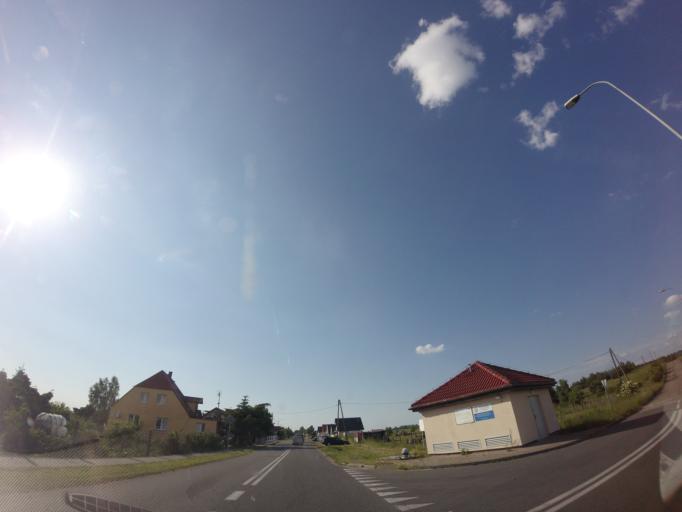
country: PL
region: West Pomeranian Voivodeship
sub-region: Powiat mysliborski
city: Barlinek
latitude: 53.0064
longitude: 15.1937
